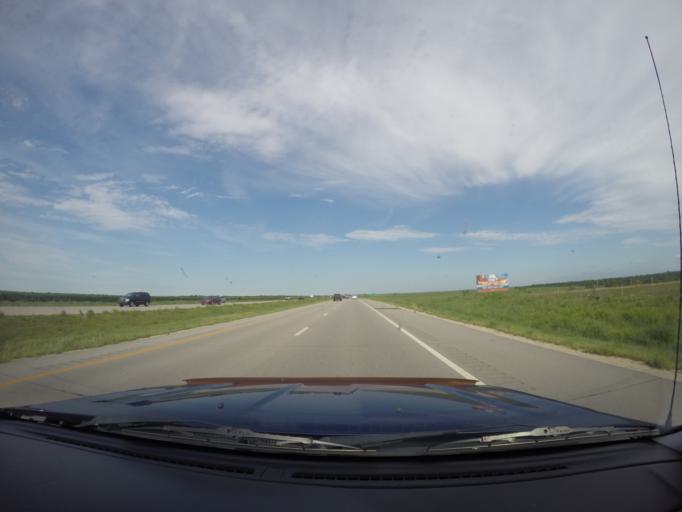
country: US
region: Kansas
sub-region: Shawnee County
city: Rossville
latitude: 39.0582
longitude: -95.9342
